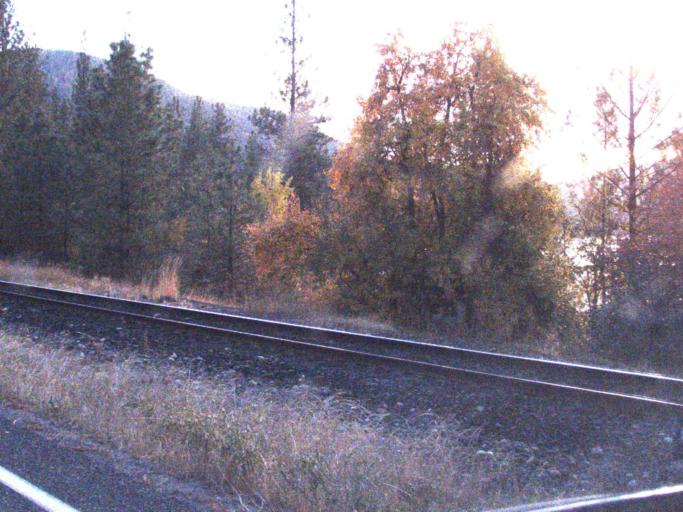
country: US
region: Washington
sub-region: Stevens County
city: Kettle Falls
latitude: 48.6862
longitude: -118.0135
